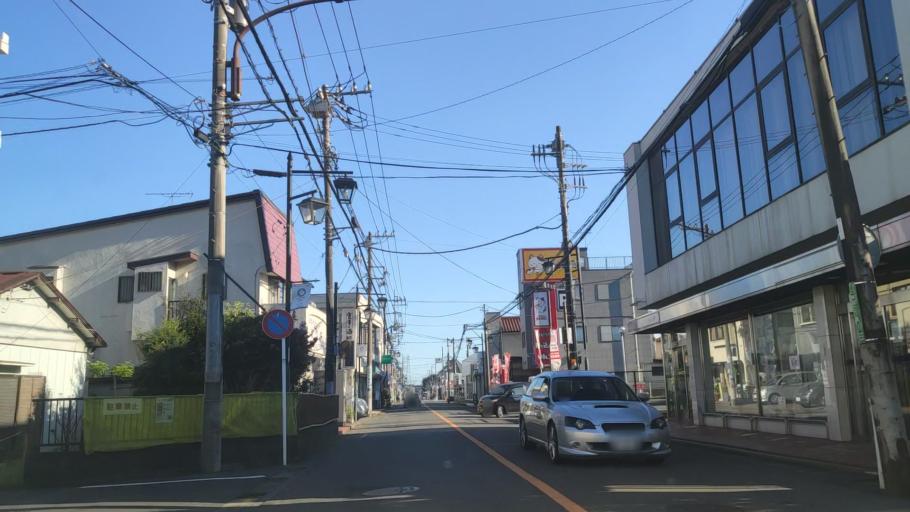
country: JP
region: Tokyo
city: Hachioji
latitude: 35.5973
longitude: 139.3206
